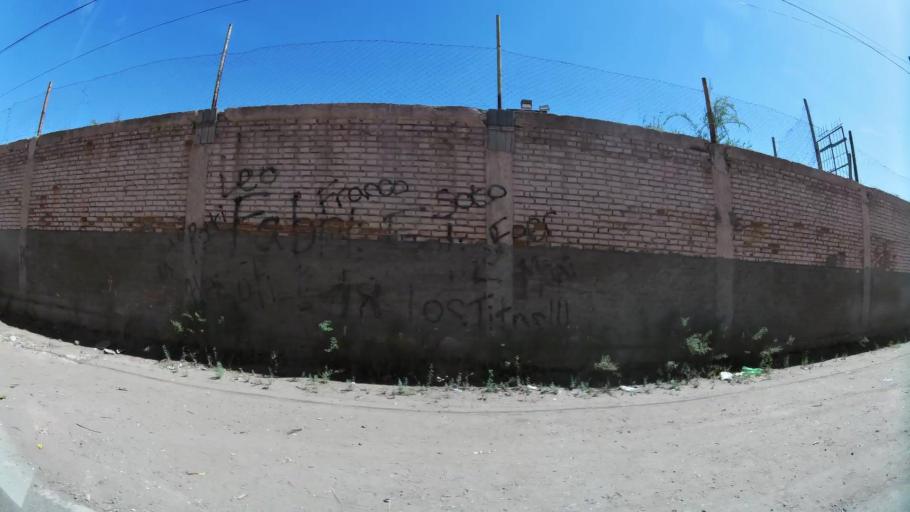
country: AR
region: Mendoza
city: Villa Nueva
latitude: -32.8698
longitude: -68.7854
